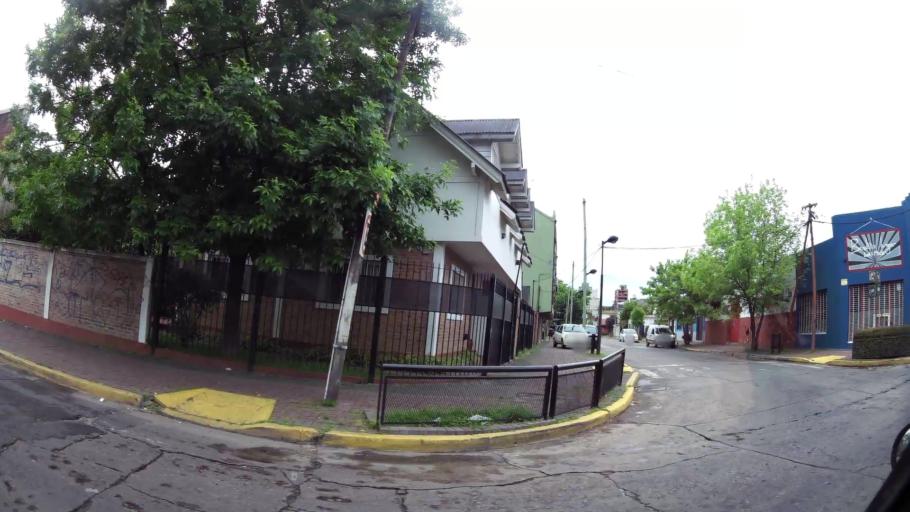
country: AR
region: Buenos Aires
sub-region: Partido de Quilmes
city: Quilmes
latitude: -34.7528
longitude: -58.2160
